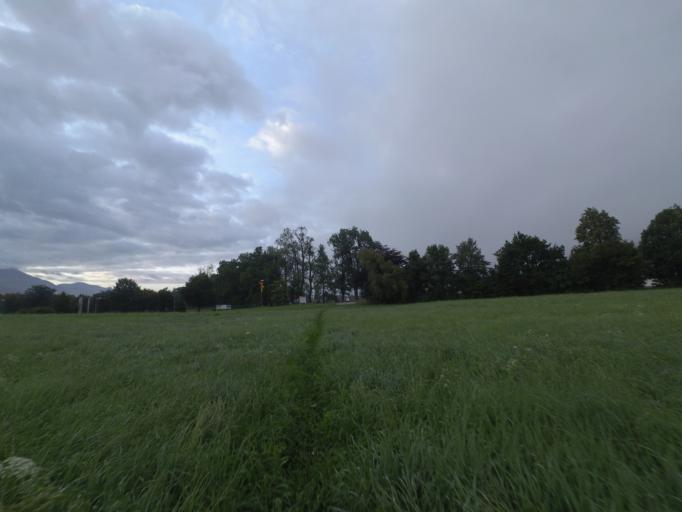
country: AT
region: Salzburg
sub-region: Politischer Bezirk Salzburg-Umgebung
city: Anif
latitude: 47.7226
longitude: 13.0654
